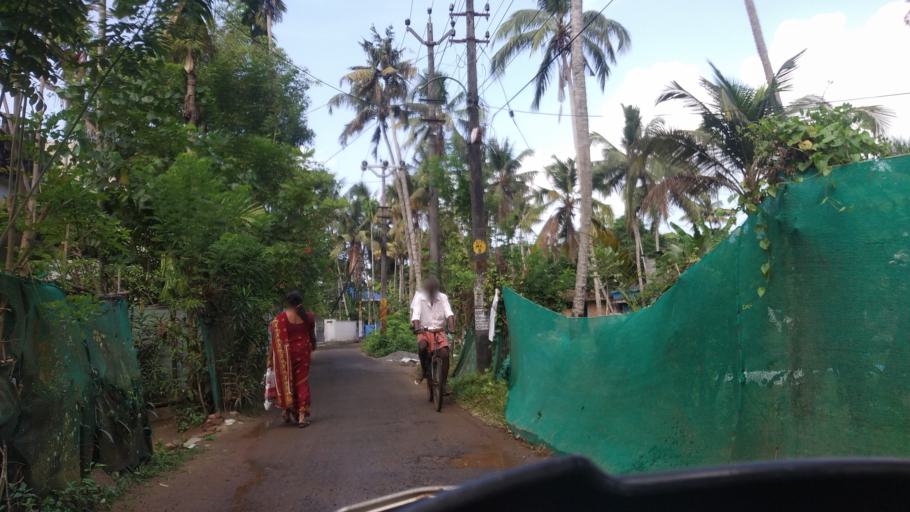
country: IN
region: Kerala
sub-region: Thrissur District
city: Kodungallur
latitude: 10.1383
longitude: 76.2178
